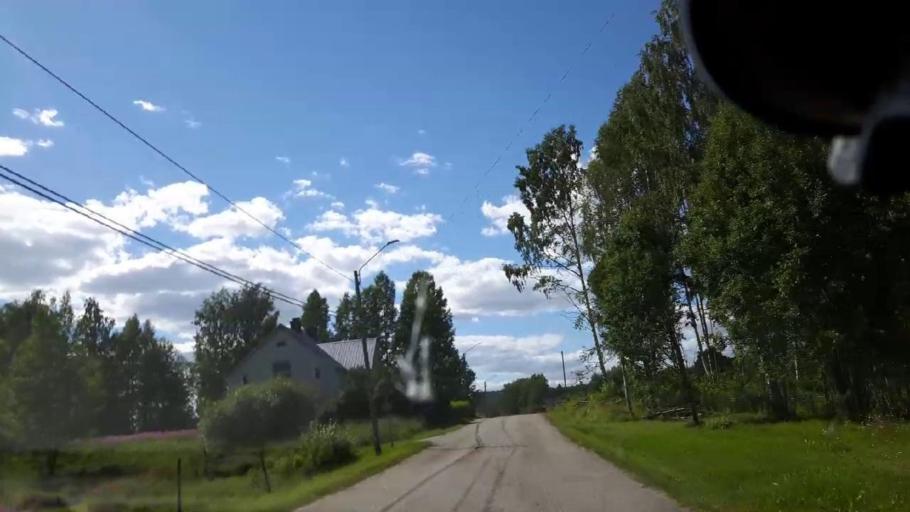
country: SE
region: Vaesternorrland
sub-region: Ange Kommun
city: Fransta
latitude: 62.7795
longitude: 16.0121
